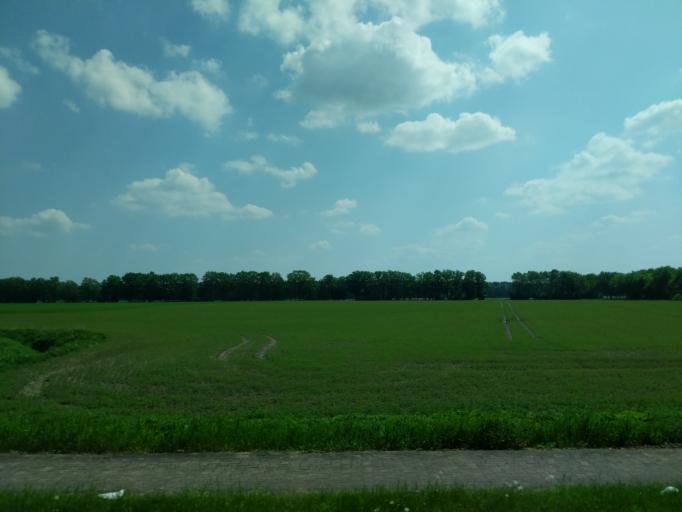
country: DE
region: Mecklenburg-Vorpommern
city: Stralendorf
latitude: 53.4931
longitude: 11.2831
